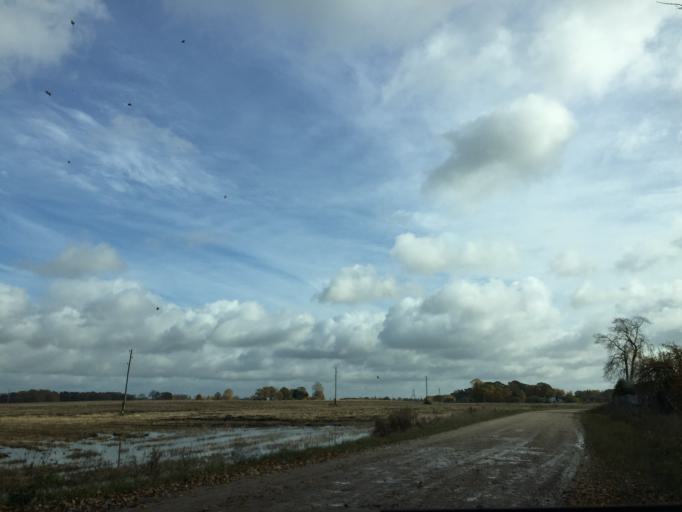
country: LV
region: Lielvarde
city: Lielvarde
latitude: 56.7213
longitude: 24.8376
